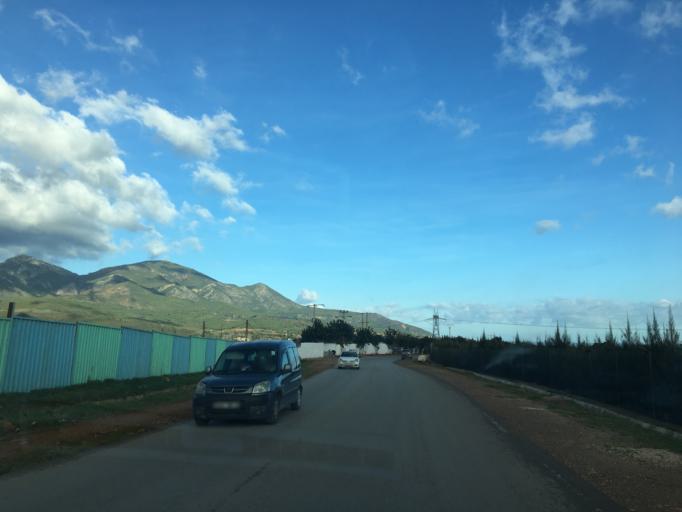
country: DZ
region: Tipaza
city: Hadjout
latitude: 36.5538
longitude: 2.4073
